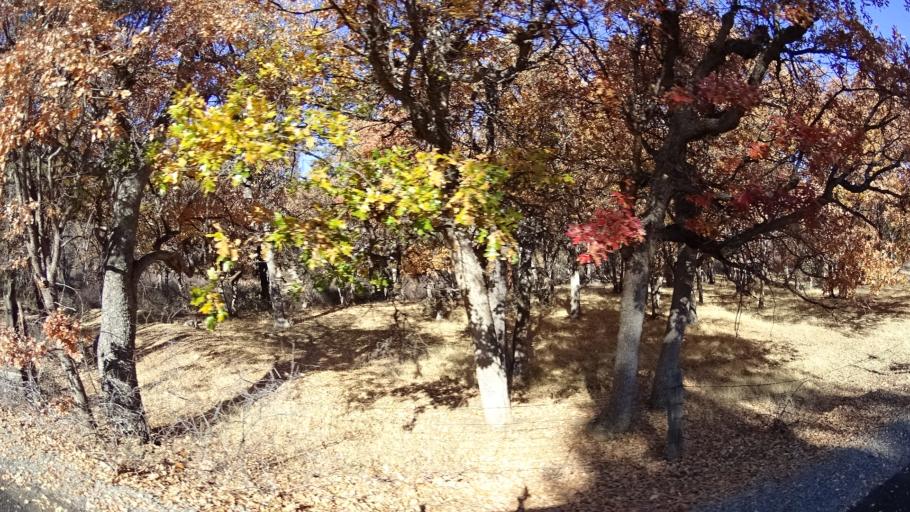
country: US
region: California
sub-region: Siskiyou County
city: Weed
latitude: 41.5037
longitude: -122.5783
